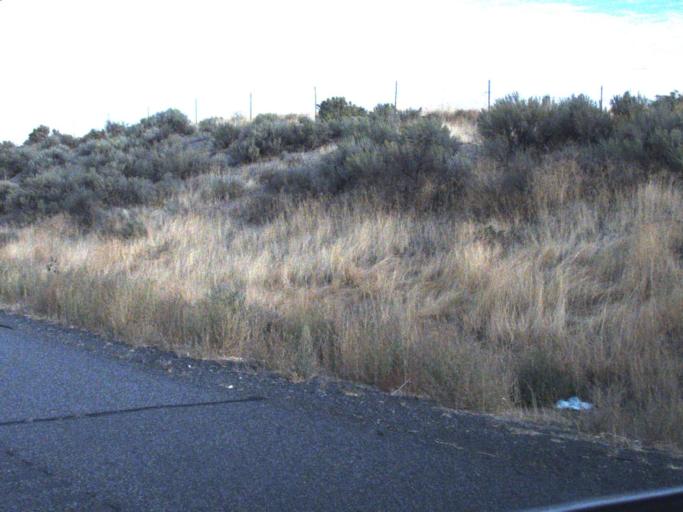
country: US
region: Washington
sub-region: Benton County
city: West Richland
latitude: 46.2556
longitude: -119.3799
